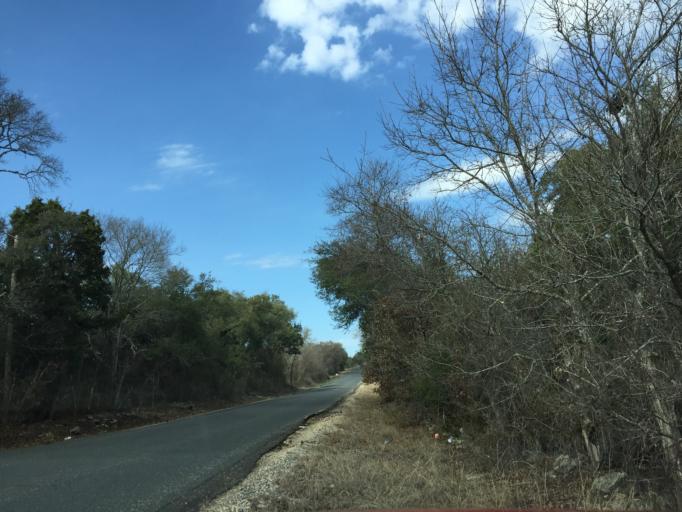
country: US
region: Texas
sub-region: Burnet County
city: Bertram
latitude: 30.7425
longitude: -97.9384
